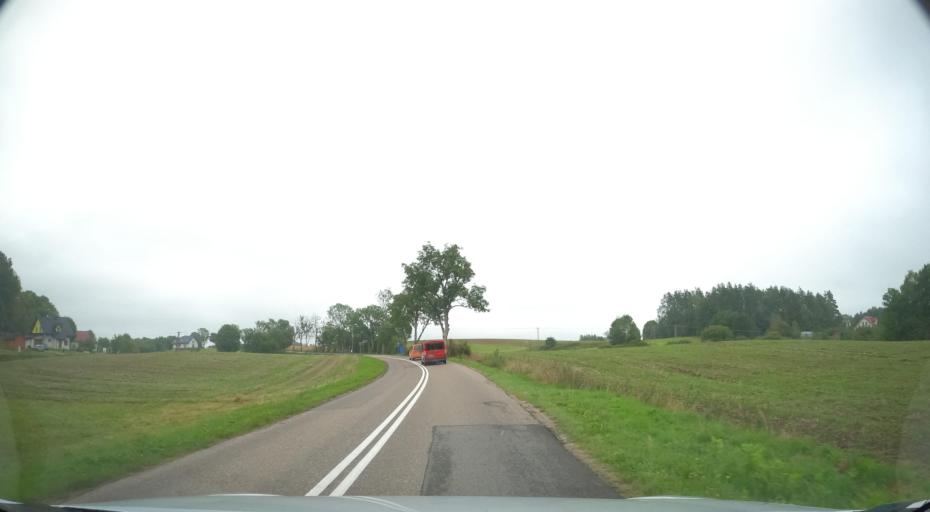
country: PL
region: Pomeranian Voivodeship
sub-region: Powiat wejherowski
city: Luzino
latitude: 54.4932
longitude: 18.1354
